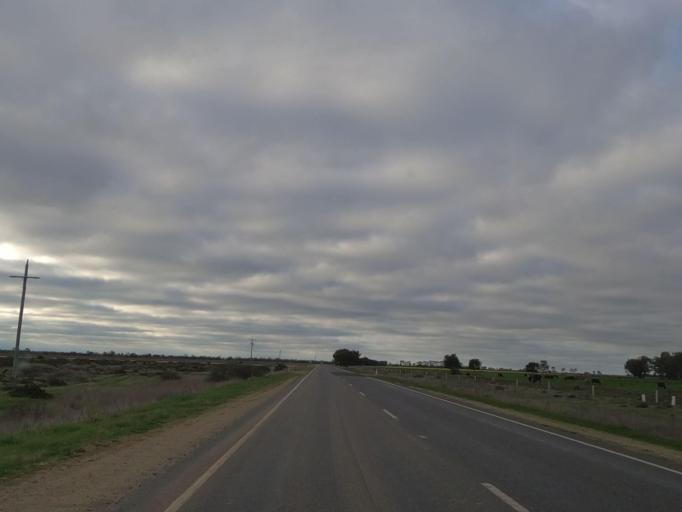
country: AU
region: Victoria
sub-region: Swan Hill
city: Swan Hill
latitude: -35.8338
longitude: 143.9429
